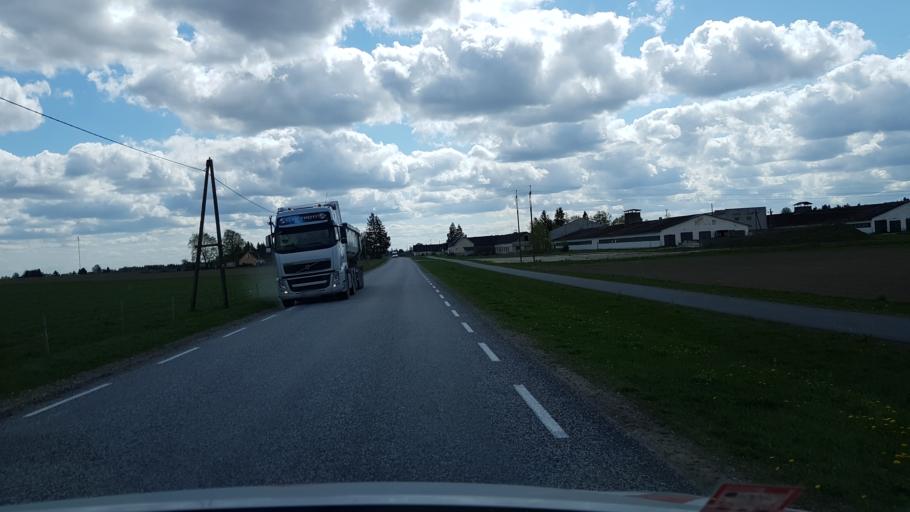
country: EE
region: Jogevamaa
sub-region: Poltsamaa linn
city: Poltsamaa
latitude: 58.6789
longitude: 25.9554
